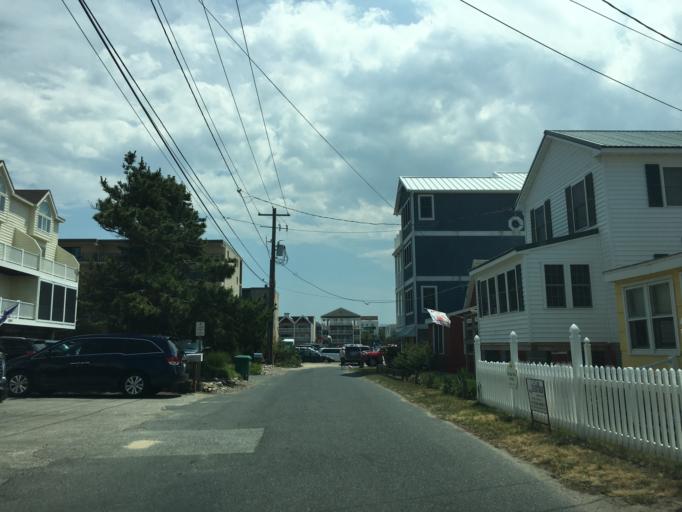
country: US
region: Delaware
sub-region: Sussex County
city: Bethany Beach
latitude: 38.4518
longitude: -75.0507
